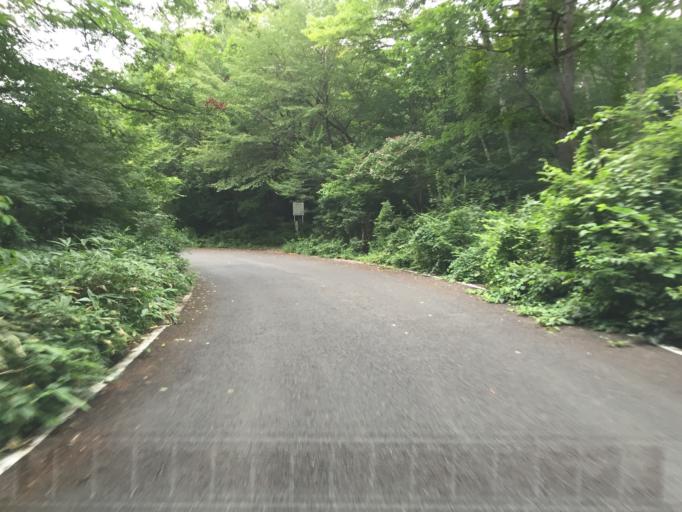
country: JP
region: Fukushima
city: Motomiya
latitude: 37.5743
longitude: 140.3230
